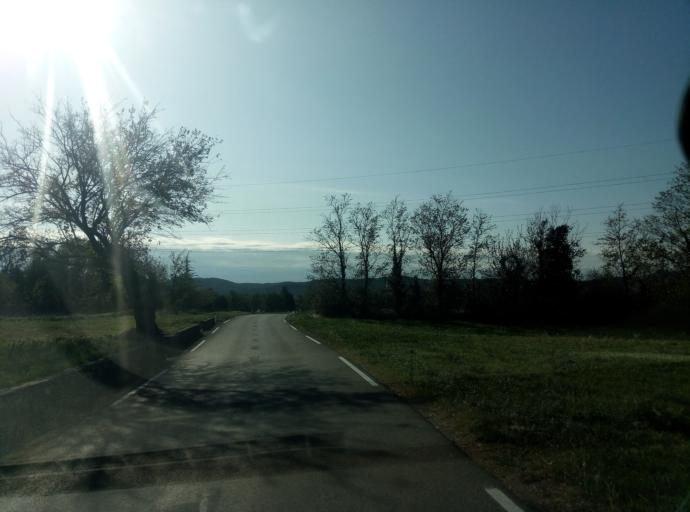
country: SI
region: Komen
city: Komen
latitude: 45.8054
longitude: 13.7178
